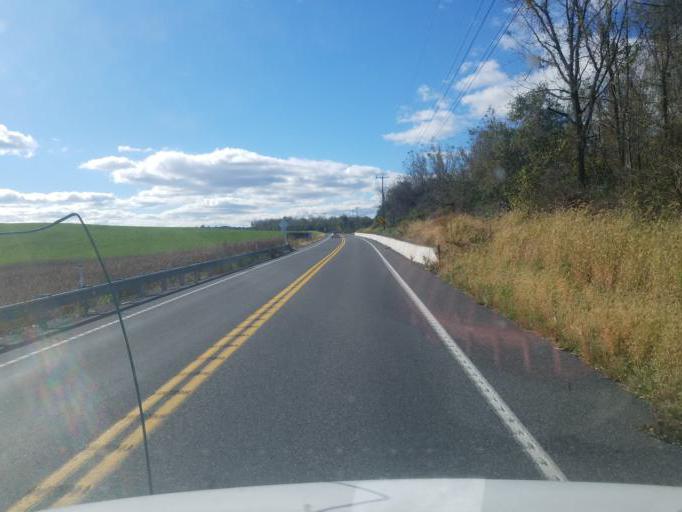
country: US
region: Pennsylvania
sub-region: Franklin County
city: Waynesboro
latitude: 39.7803
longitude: -77.5696
